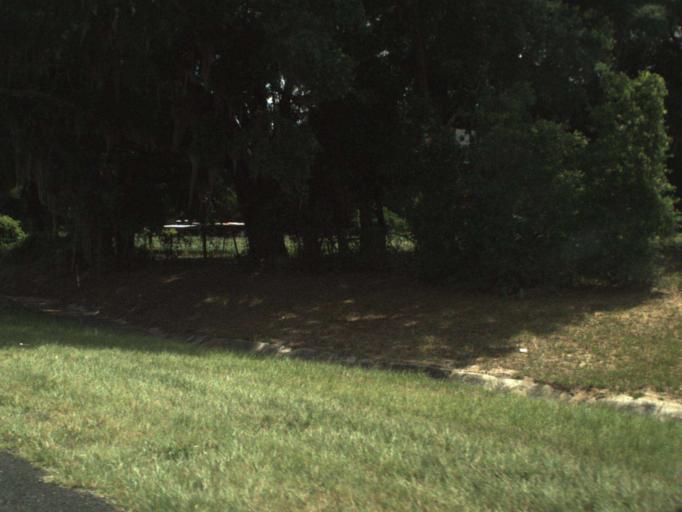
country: US
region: Florida
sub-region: Marion County
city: Ocala
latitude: 29.2837
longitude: -82.1521
